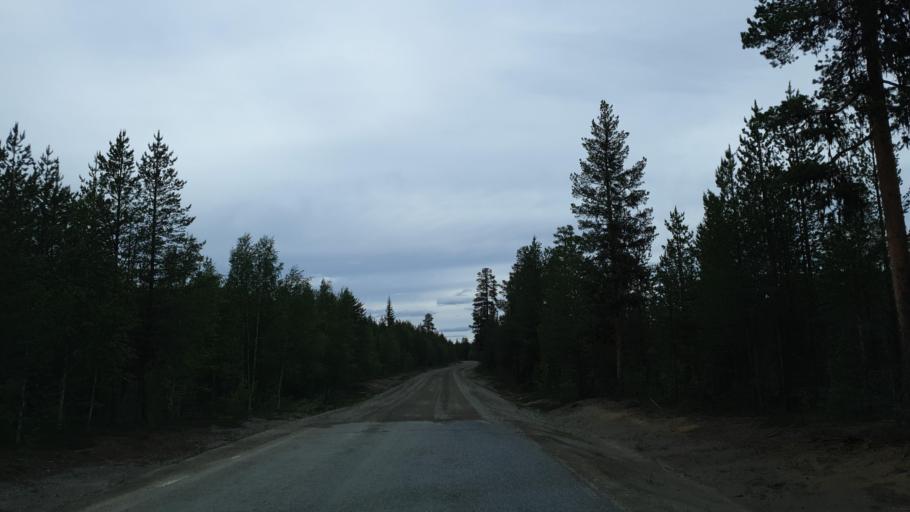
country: SE
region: Vaesterbotten
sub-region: Sorsele Kommun
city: Sorsele
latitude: 65.5519
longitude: 17.5080
